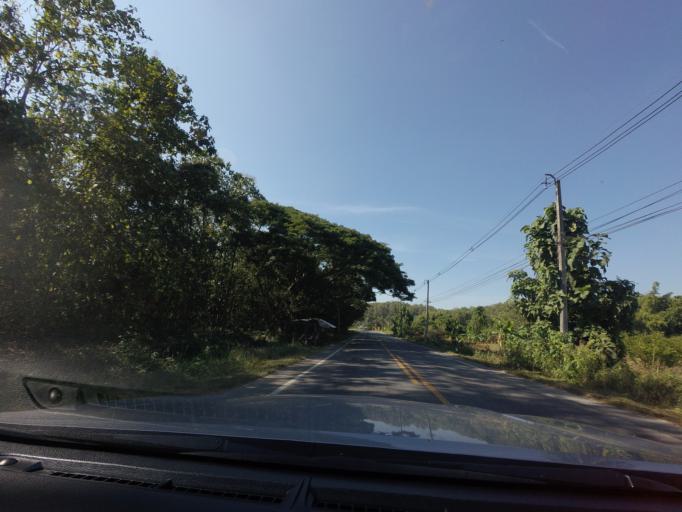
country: TH
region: Sukhothai
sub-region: Amphoe Si Satchanalai
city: Si Satchanalai
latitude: 17.6299
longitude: 99.6989
